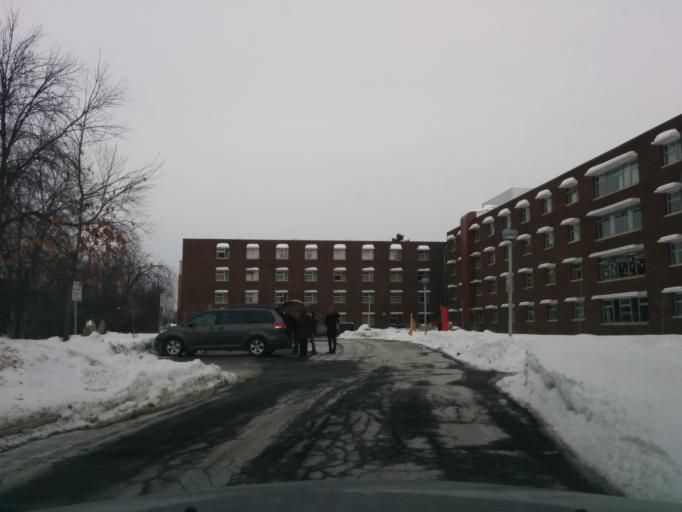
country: CA
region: Ontario
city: Ottawa
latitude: 45.3862
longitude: -75.6989
